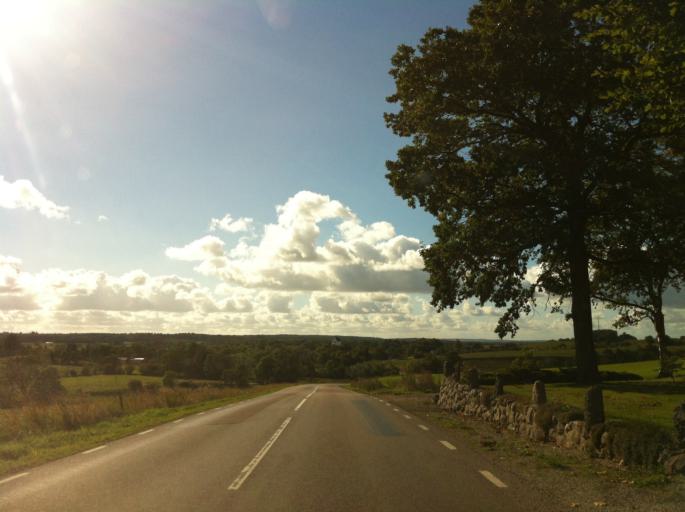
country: SE
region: Skane
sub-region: Sjobo Kommun
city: Sjoebo
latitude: 55.6440
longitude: 13.7926
